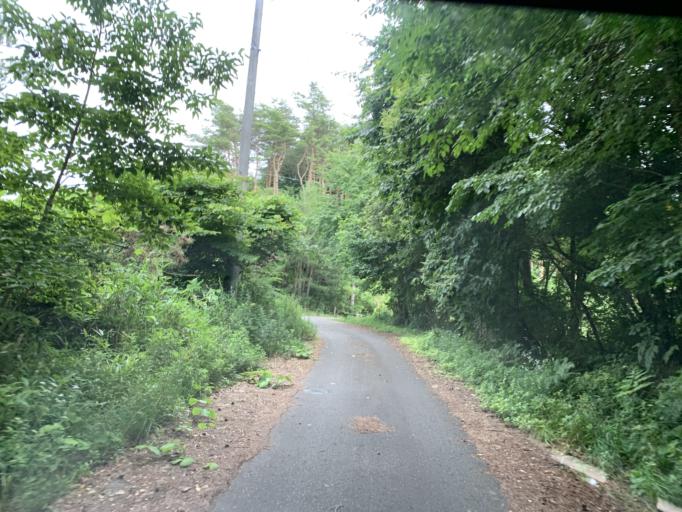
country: JP
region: Iwate
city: Ichinoseki
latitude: 38.8294
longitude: 141.2243
